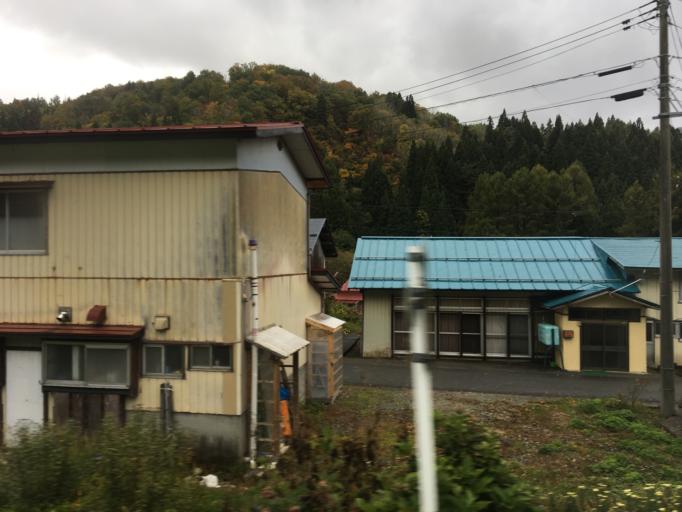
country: JP
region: Yamagata
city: Nagai
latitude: 38.0280
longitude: 139.8732
